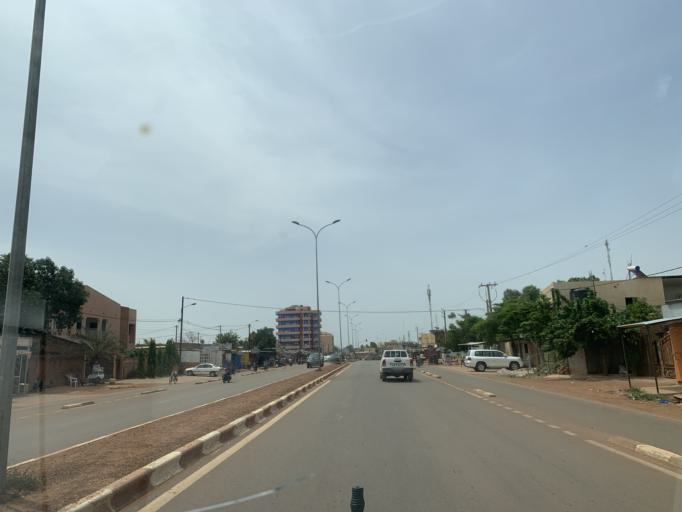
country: BF
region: Centre
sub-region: Kadiogo Province
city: Ouagadougou
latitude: 12.3392
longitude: -1.5111
